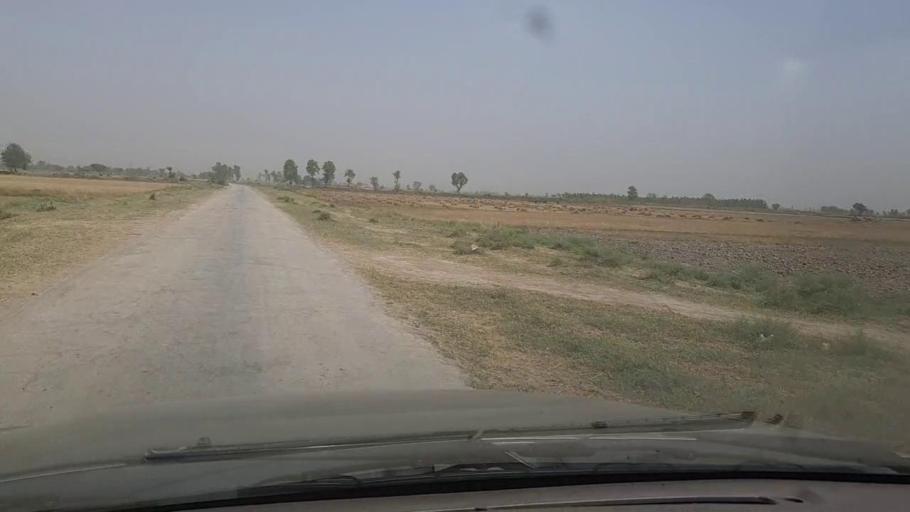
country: PK
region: Sindh
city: Madeji
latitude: 27.8147
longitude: 68.3979
